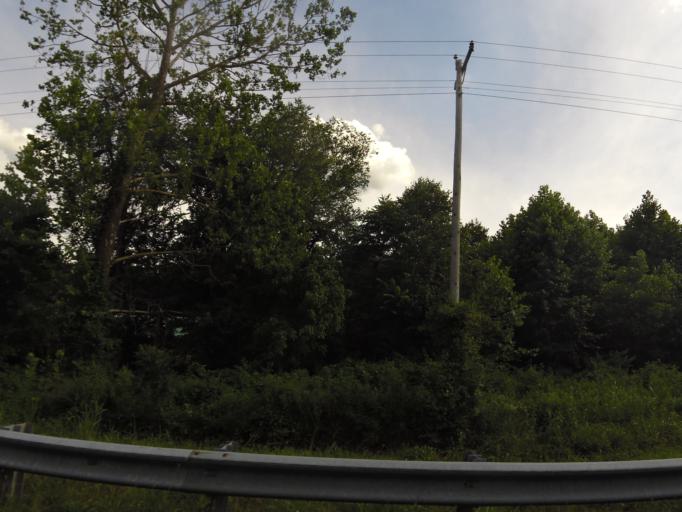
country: US
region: Tennessee
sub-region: Carroll County
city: Bruceton
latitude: 36.0366
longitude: -88.2923
